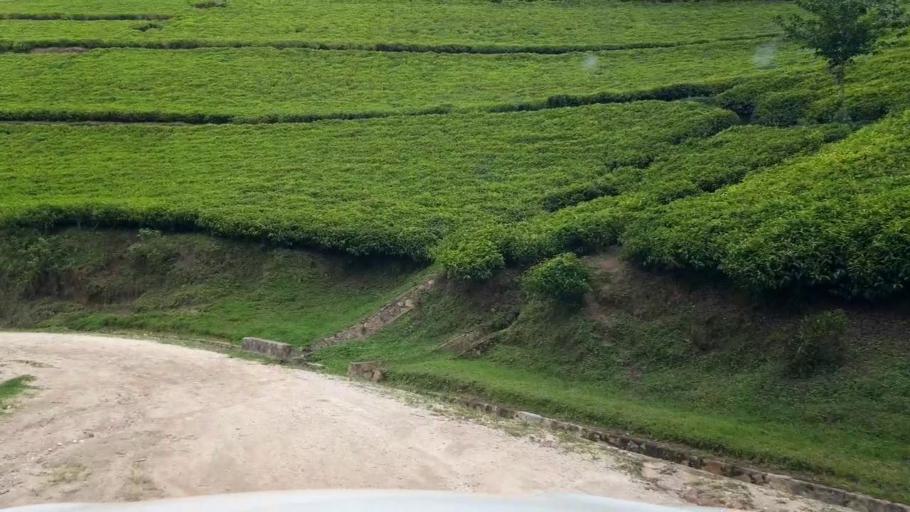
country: RW
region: Western Province
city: Kibuye
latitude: -1.8656
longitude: 29.5509
